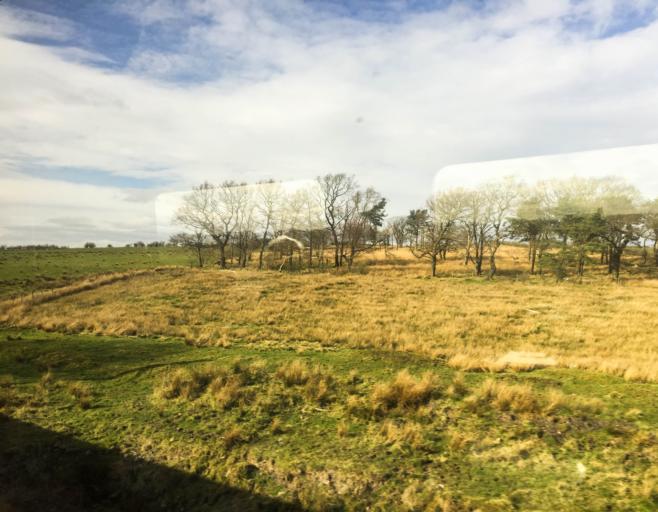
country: GB
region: Scotland
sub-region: North Lanarkshire
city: Chryston
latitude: 55.8884
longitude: -4.0972
